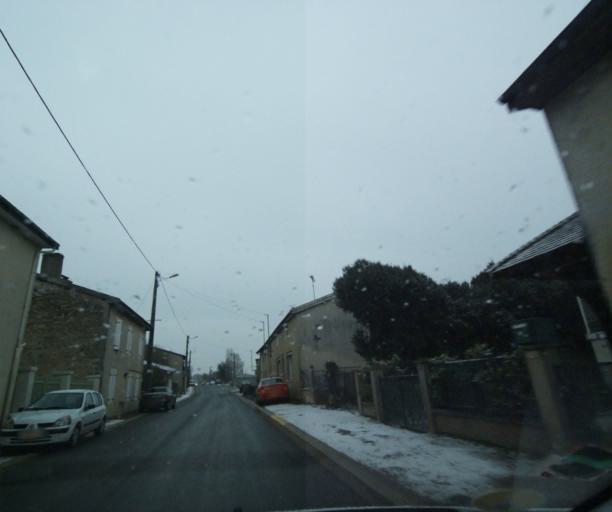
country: FR
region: Champagne-Ardenne
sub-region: Departement de la Haute-Marne
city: Wassy
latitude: 48.4703
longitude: 4.9709
